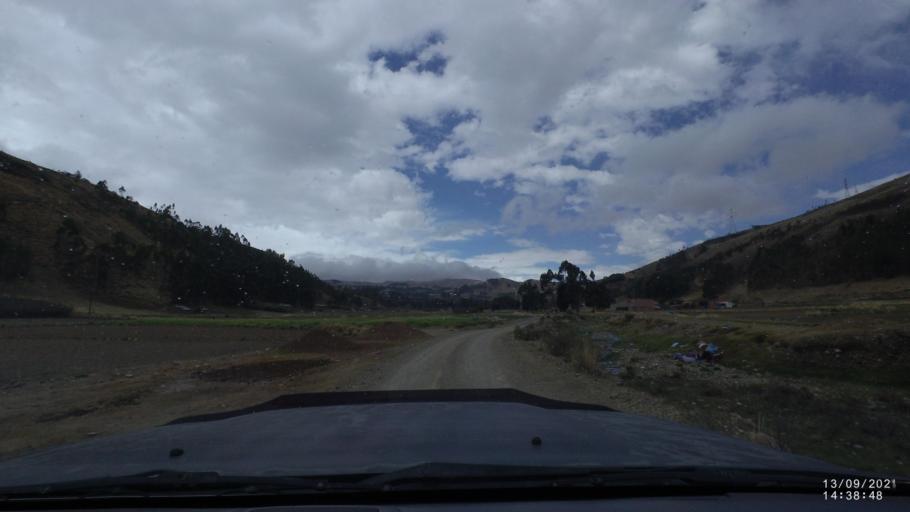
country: BO
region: Cochabamba
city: Colomi
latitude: -17.3695
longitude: -65.8298
